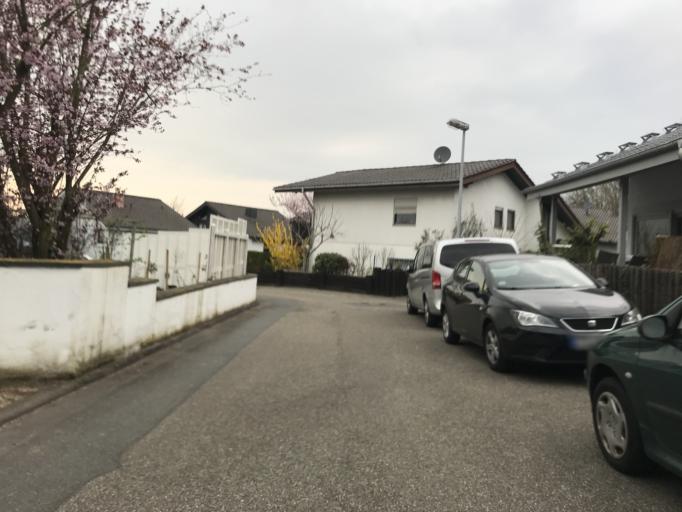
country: DE
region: Rheinland-Pfalz
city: Klein-Winternheim
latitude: 49.9427
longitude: 8.2229
